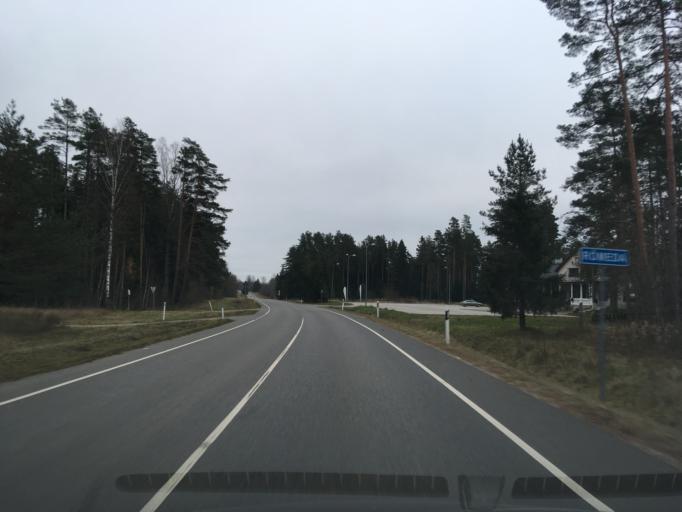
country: EE
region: Laeaene-Virumaa
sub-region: Kadrina vald
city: Kadrina
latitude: 59.4526
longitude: 26.0284
